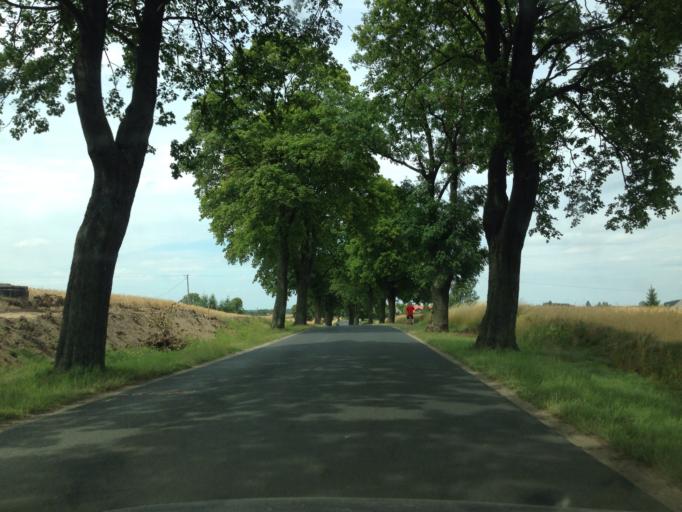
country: PL
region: Kujawsko-Pomorskie
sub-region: Powiat brodnicki
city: Brodnica
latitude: 53.3122
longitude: 19.3889
